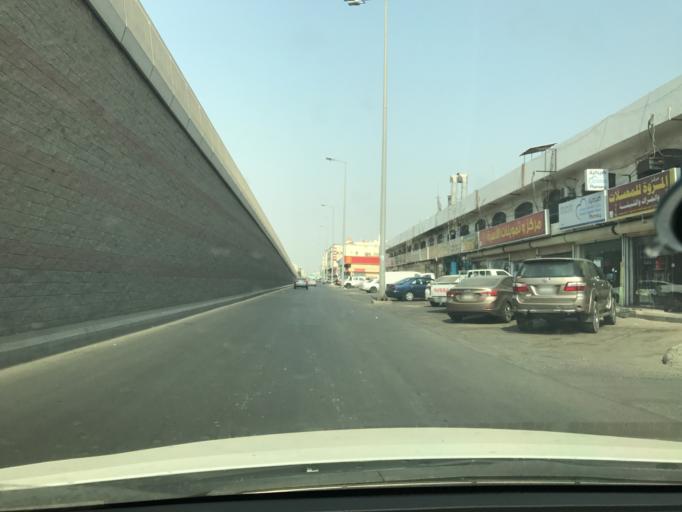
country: SA
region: Makkah
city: Jeddah
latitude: 21.6197
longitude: 39.1865
